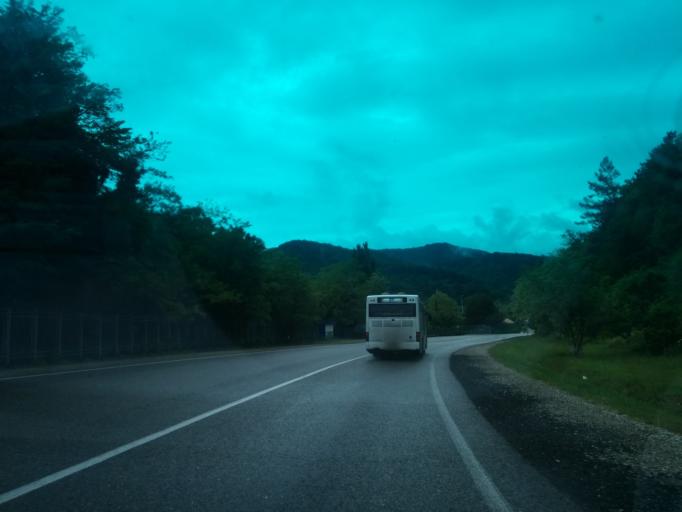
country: RU
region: Krasnodarskiy
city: Nebug
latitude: 44.1602
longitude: 39.0013
